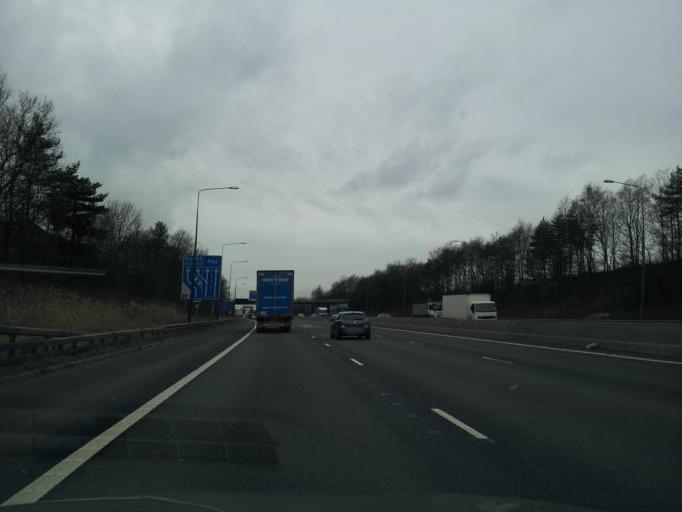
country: GB
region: England
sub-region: Warrington
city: Culcheth
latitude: 53.4327
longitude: -2.5282
